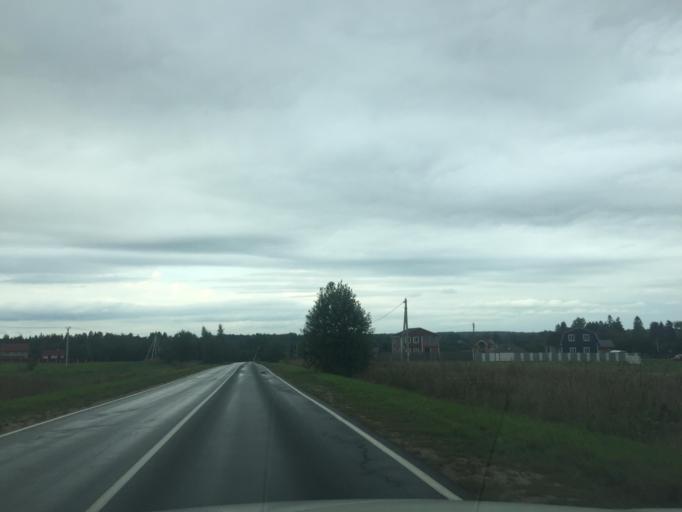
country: RU
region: Leningrad
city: Siverskiy
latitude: 59.3364
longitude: 30.0288
